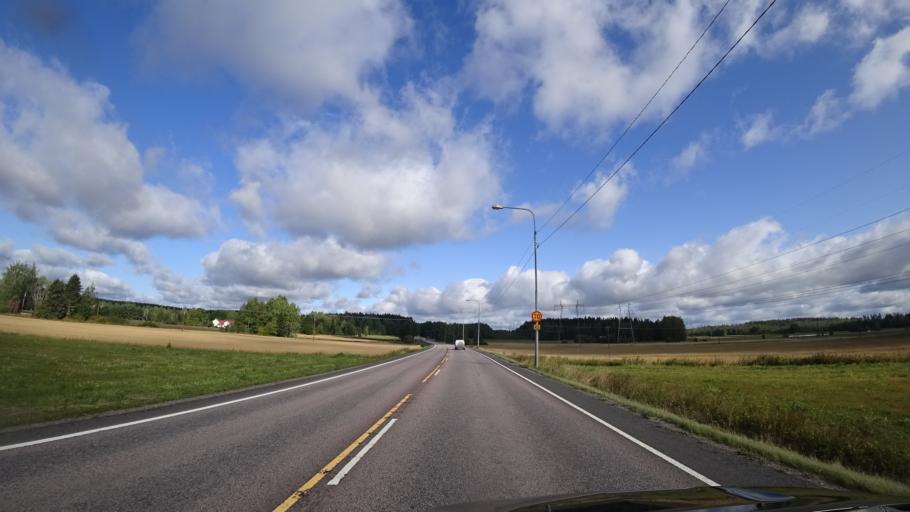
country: FI
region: Uusimaa
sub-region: Helsinki
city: Hyvinge
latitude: 60.5261
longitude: 24.9243
